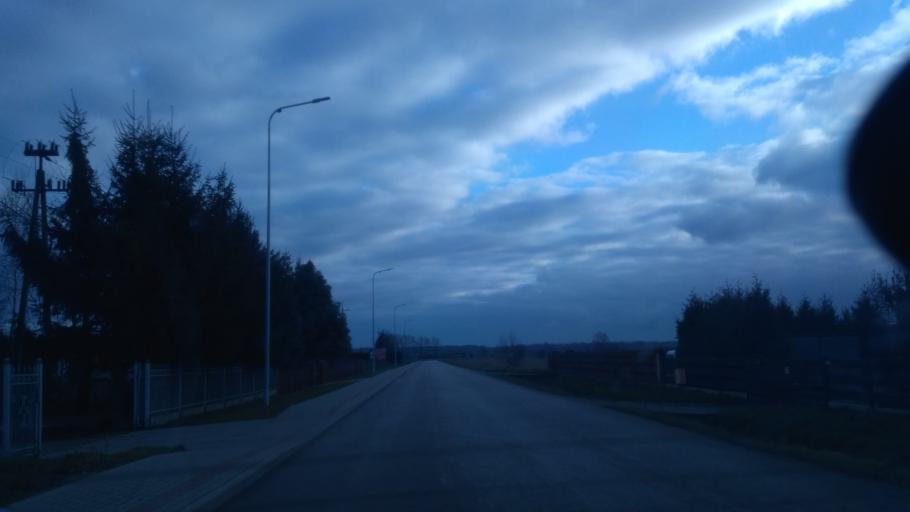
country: PL
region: Subcarpathian Voivodeship
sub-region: Powiat lancucki
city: Czarna
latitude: 50.0994
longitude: 22.1574
